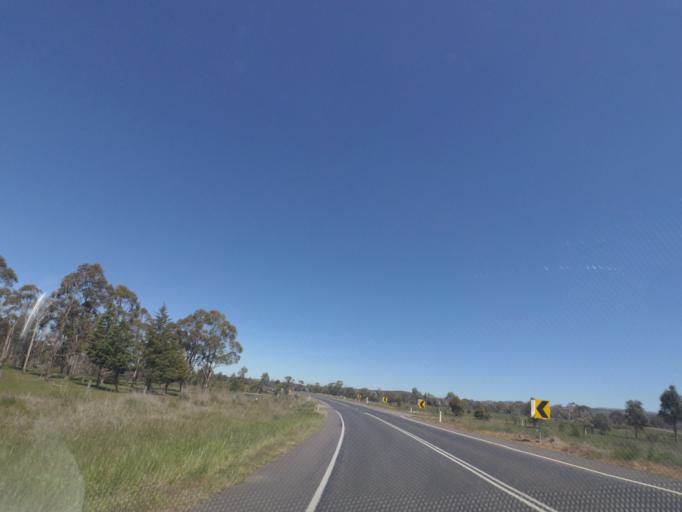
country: AU
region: Victoria
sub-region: Hume
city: Craigieburn
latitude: -37.2893
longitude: 144.8879
